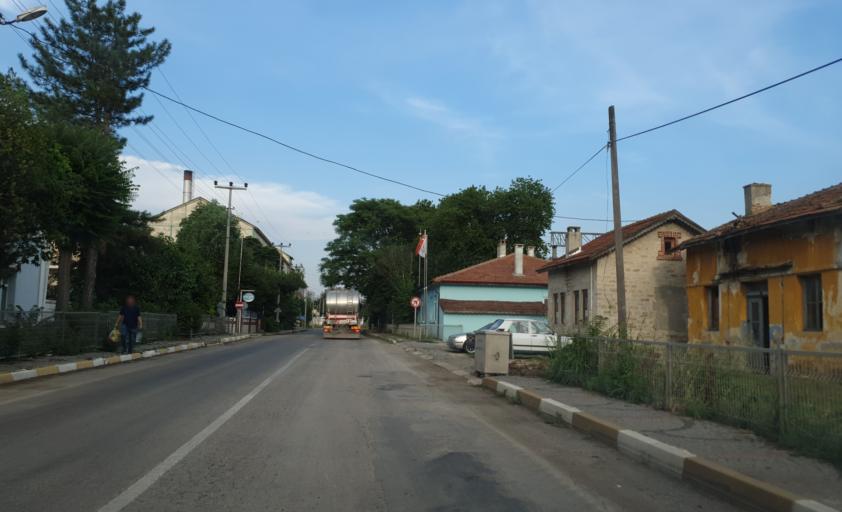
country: TR
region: Kirklareli
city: Babaeski
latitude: 41.3667
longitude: 27.1411
